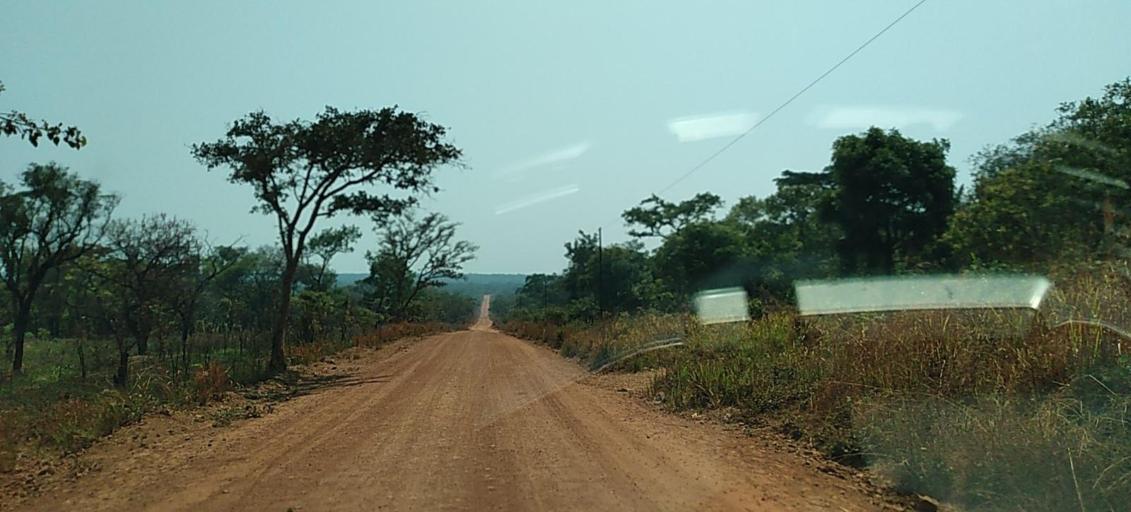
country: ZM
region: North-Western
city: Kansanshi
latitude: -12.0034
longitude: 26.5855
